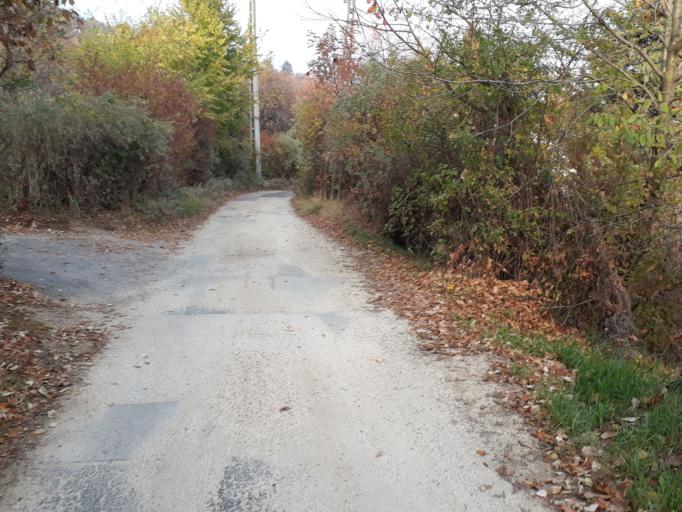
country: HU
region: Pest
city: Budaors
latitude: 47.4748
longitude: 18.9726
